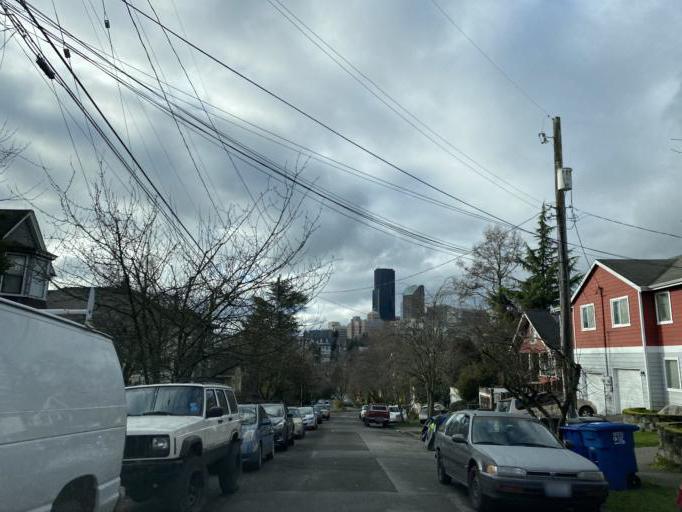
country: US
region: Washington
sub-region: King County
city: Seattle
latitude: 47.6036
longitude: -122.3117
